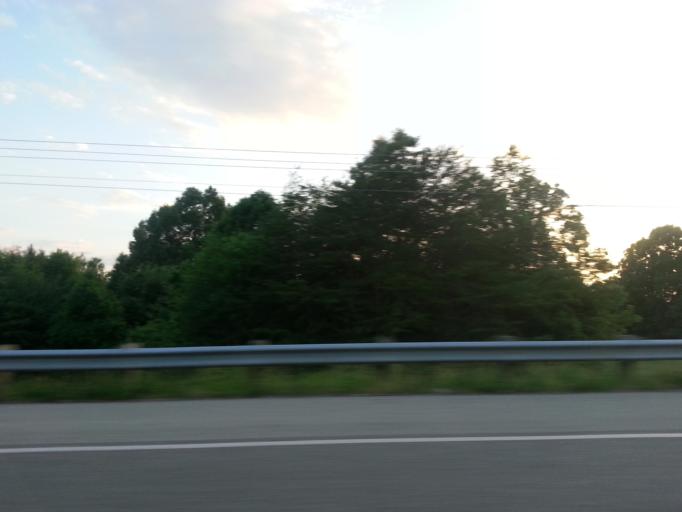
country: US
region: Tennessee
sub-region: Monroe County
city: Madisonville
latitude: 35.4001
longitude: -84.3520
